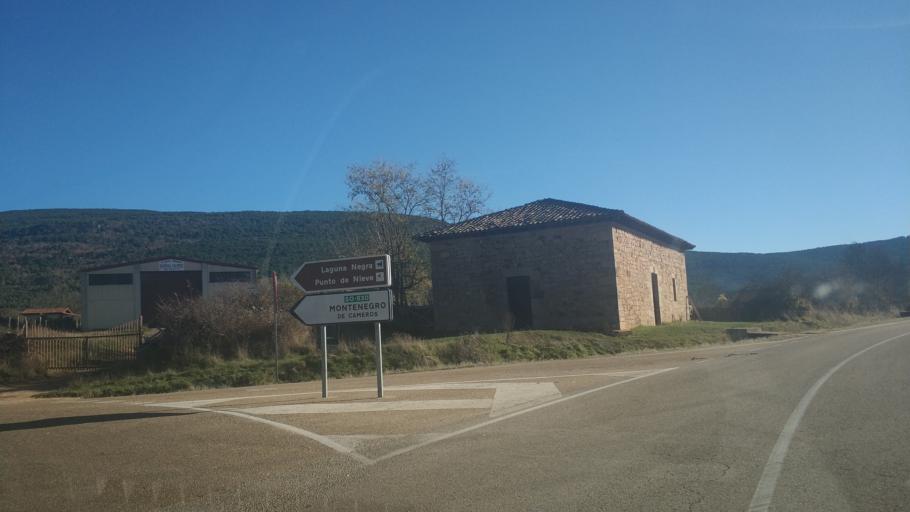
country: ES
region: Castille and Leon
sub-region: Provincia de Soria
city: Vinuesa
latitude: 41.9118
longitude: -2.7555
